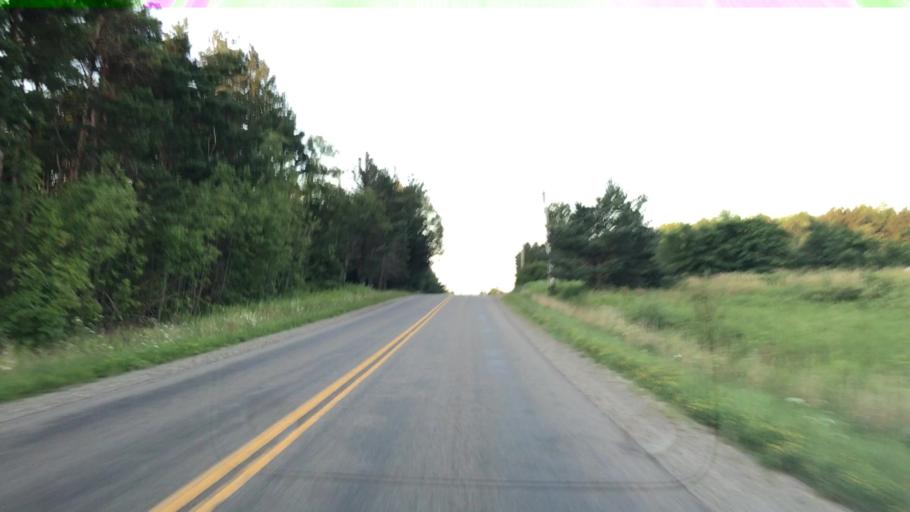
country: US
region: New York
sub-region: Chautauqua County
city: Brocton
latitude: 42.2972
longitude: -79.4044
